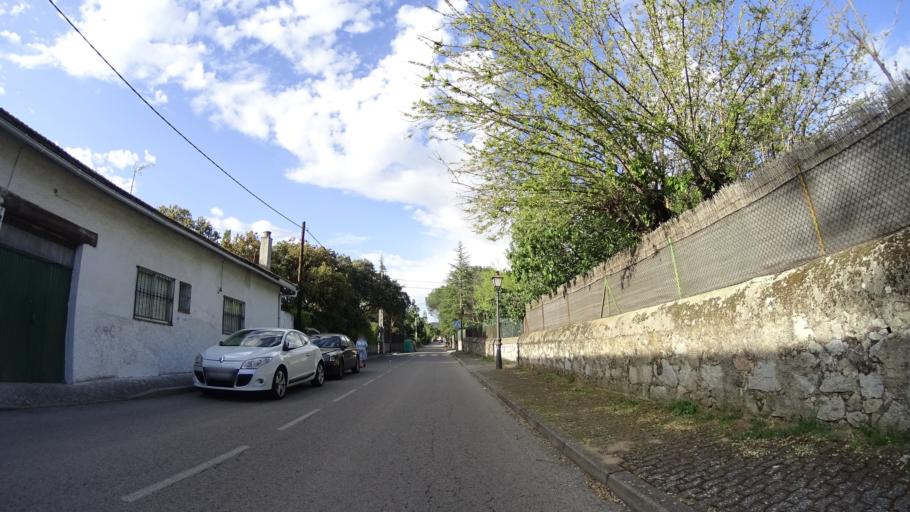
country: ES
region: Madrid
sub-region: Provincia de Madrid
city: Torrelodones
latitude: 40.5836
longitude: -3.9561
